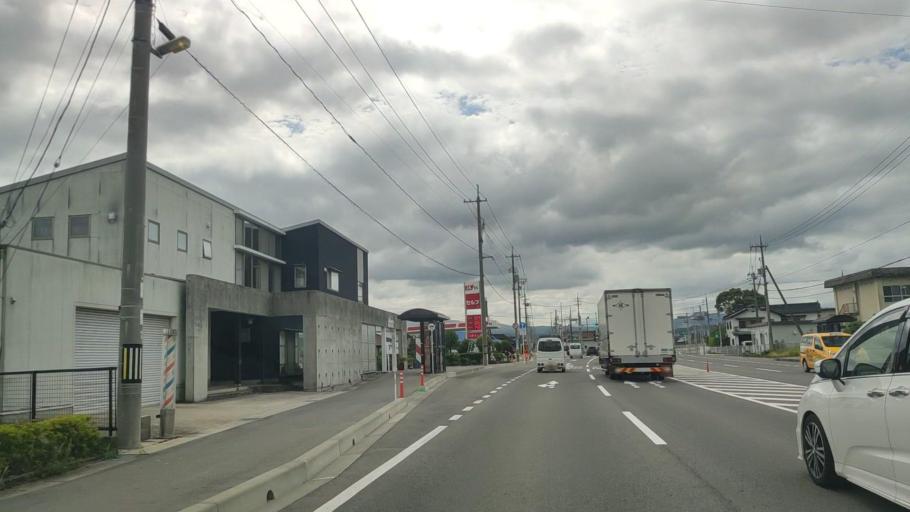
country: JP
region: Tottori
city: Yonago
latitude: 35.3987
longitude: 133.3780
